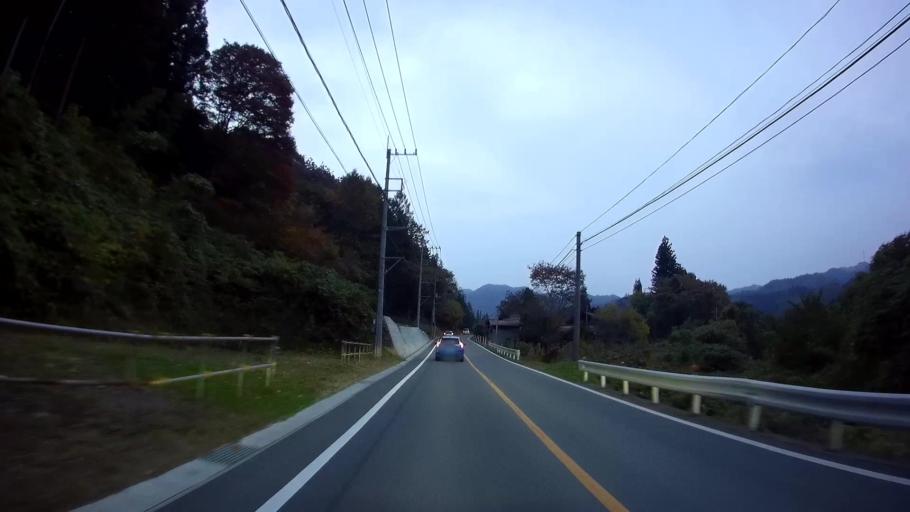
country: JP
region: Gunma
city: Nakanojomachi
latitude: 36.5399
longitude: 138.7905
